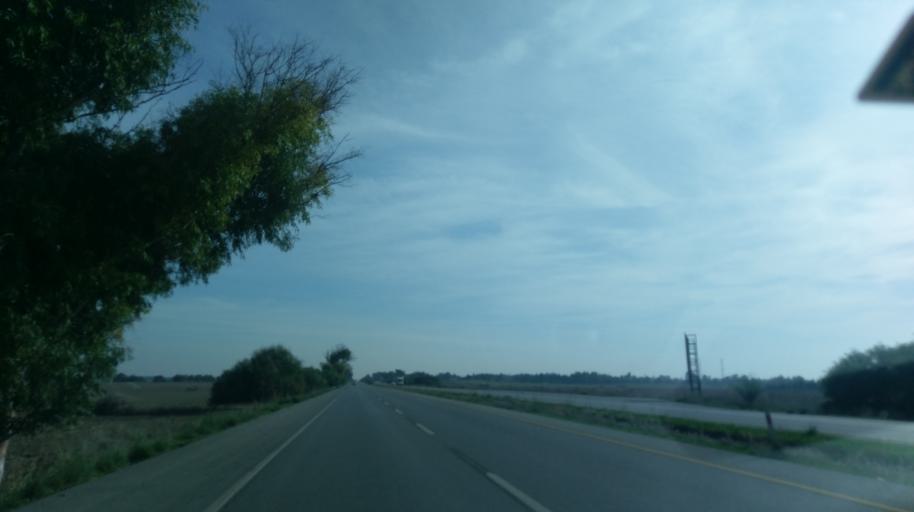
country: CY
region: Larnaka
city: Athienou
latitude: 35.2095
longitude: 33.5742
